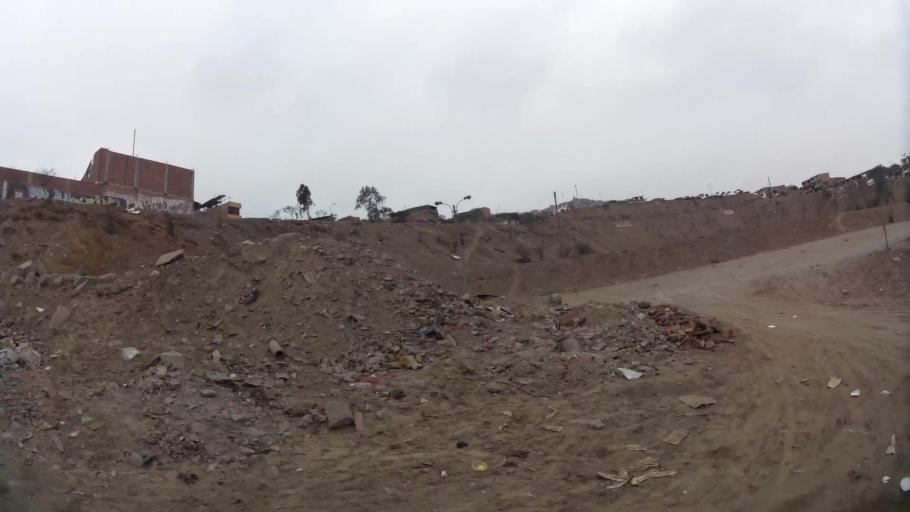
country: PE
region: Lima
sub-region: Lima
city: Surco
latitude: -12.1753
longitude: -76.9615
